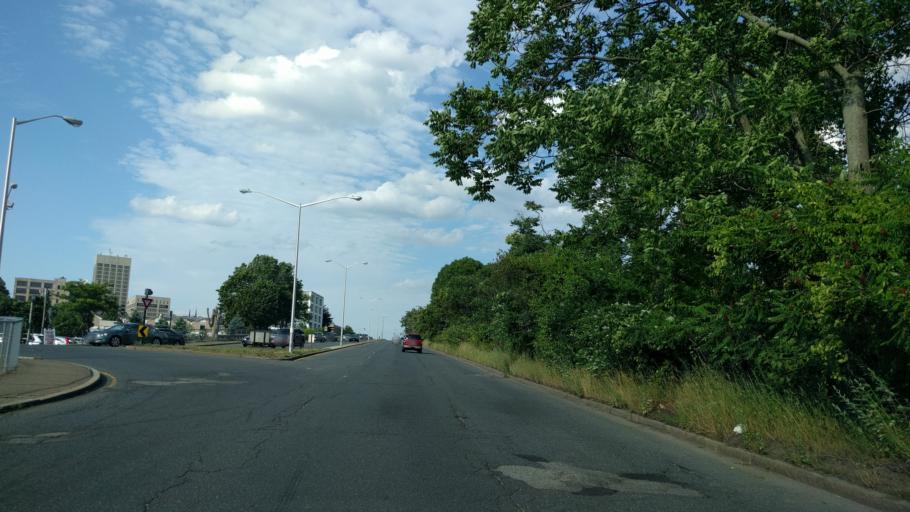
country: US
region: Massachusetts
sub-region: Worcester County
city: Worcester
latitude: 42.2563
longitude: -71.8043
